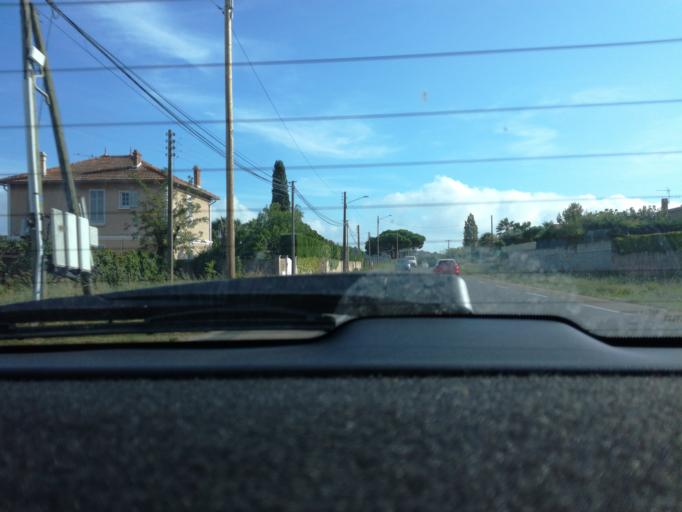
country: FR
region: Provence-Alpes-Cote d'Azur
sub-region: Departement du Var
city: Hyeres
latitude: 43.0936
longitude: 6.1307
